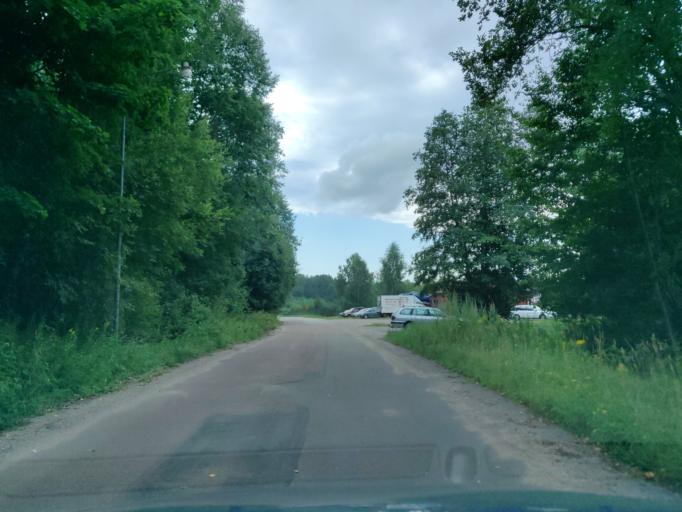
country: SE
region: Vaermland
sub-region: Munkfors Kommun
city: Munkfors
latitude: 59.8550
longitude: 13.5595
